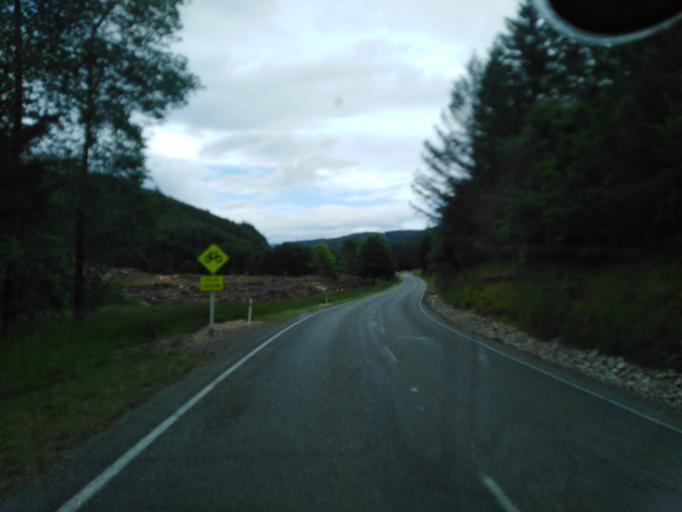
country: NZ
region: Tasman
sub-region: Tasman District
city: Wakefield
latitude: -41.4863
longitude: 172.8892
